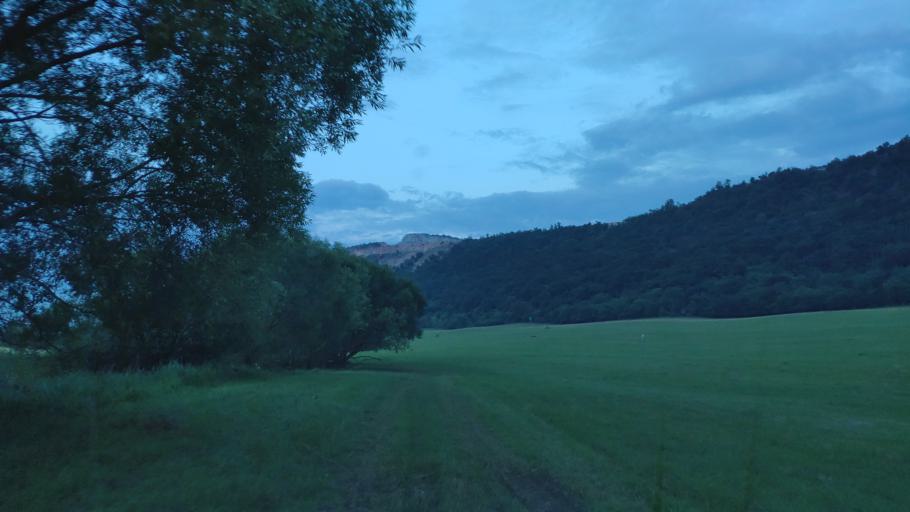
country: SK
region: Kosicky
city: Medzev
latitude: 48.5824
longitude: 20.7950
